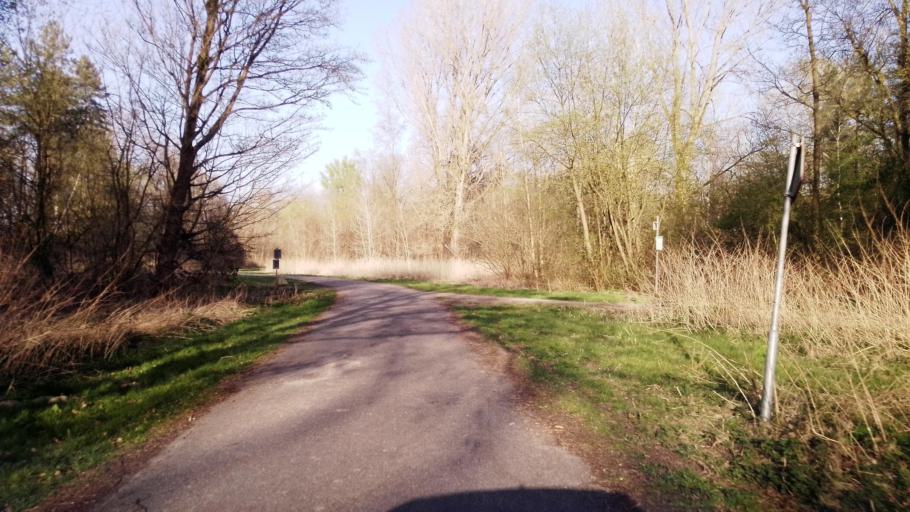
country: NL
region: Gelderland
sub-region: Gemeente Elburg
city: Elburg
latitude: 52.4509
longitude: 5.7766
